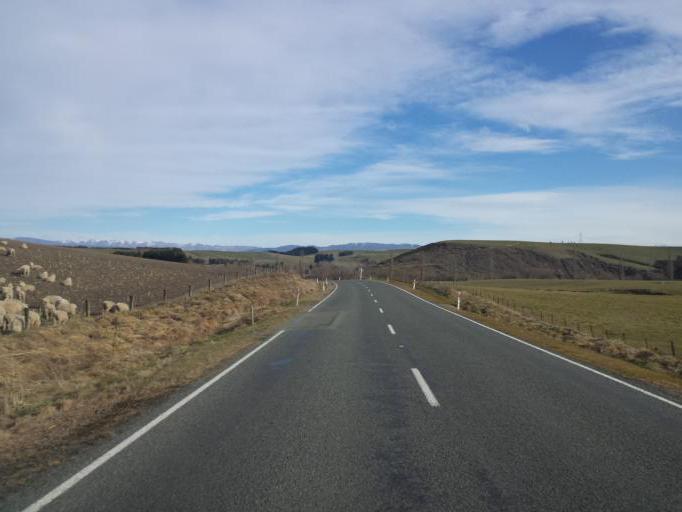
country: NZ
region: Canterbury
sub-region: Timaru District
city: Pleasant Point
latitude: -44.1197
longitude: 171.0569
